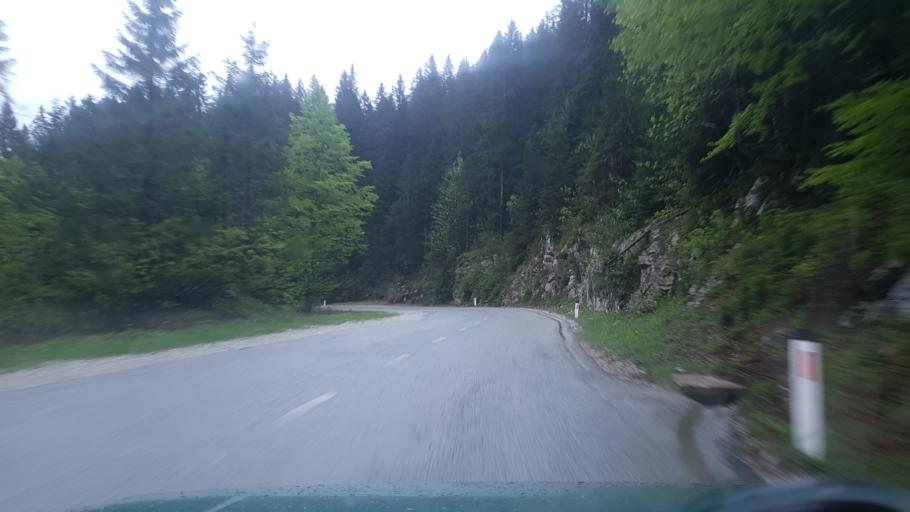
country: SI
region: Bohinj
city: Bohinjska Bistrica
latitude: 46.2391
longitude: 14.0138
